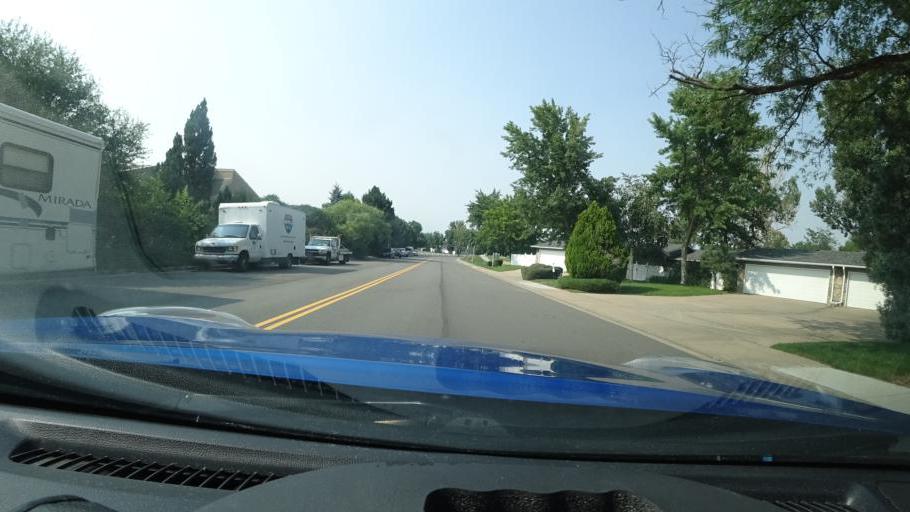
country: US
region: Colorado
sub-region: Adams County
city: Aurora
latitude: 39.6660
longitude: -104.8357
